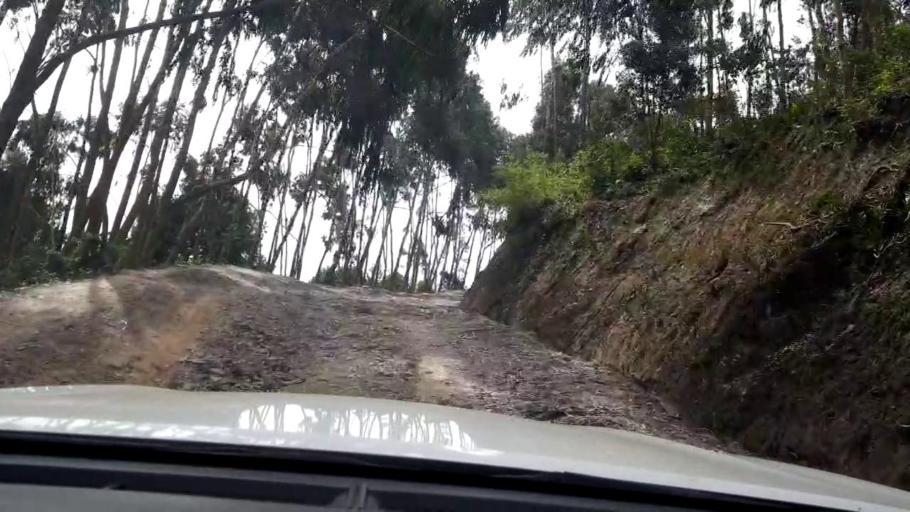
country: RW
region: Western Province
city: Kibuye
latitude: -1.8722
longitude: 29.4517
